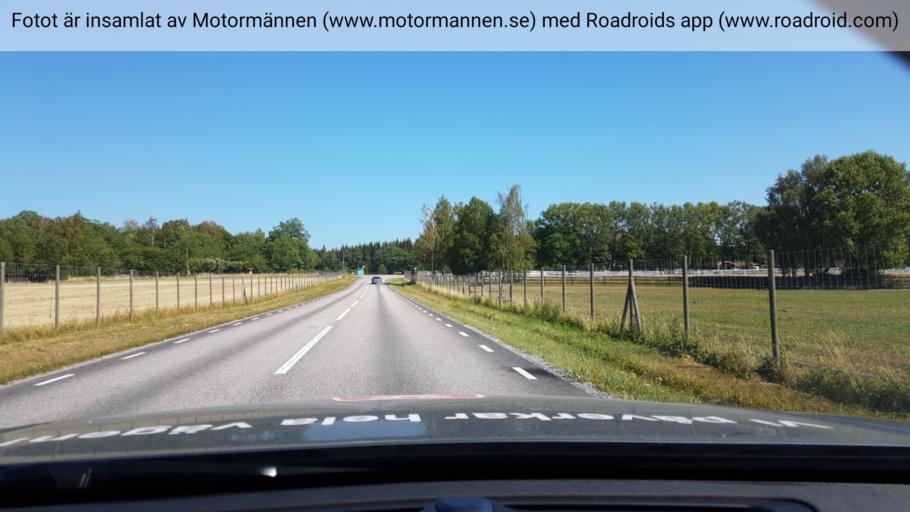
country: SE
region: Stockholm
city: Stenhamra
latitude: 59.3240
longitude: 17.6327
